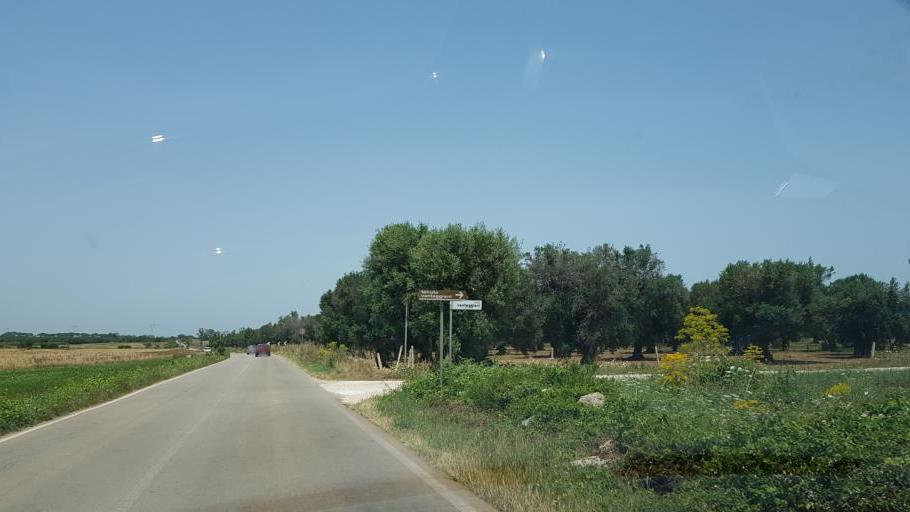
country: IT
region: Apulia
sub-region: Provincia di Lecce
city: Porto Cesareo
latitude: 40.3284
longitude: 17.8530
